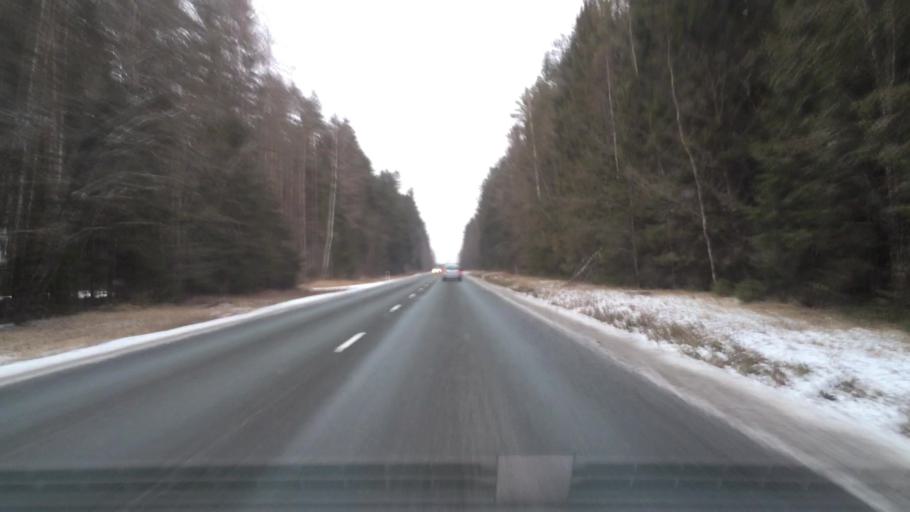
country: LV
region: Valmieras Rajons
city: Valmiera
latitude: 57.5018
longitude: 25.4189
